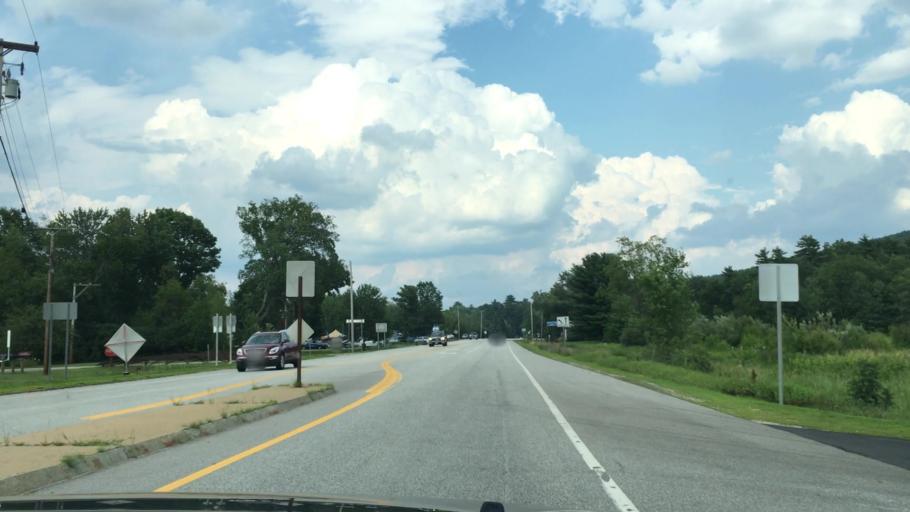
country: US
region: New Hampshire
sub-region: Belknap County
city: Gilford
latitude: 43.5778
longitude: -71.3998
